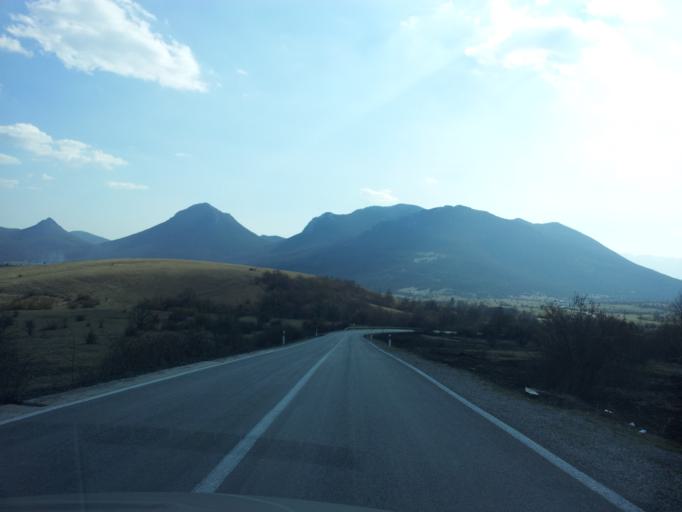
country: HR
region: Zadarska
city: Gracac
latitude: 44.4825
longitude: 15.7308
